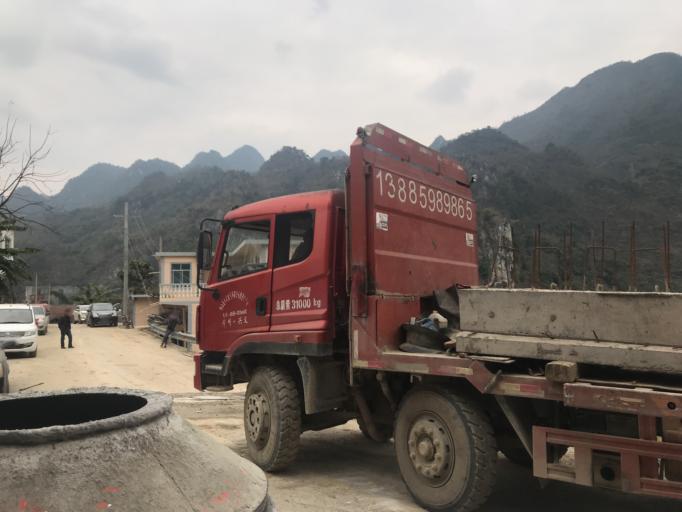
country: CN
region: Guangxi Zhuangzu Zizhiqu
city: Xinzhou
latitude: 25.1113
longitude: 105.8584
